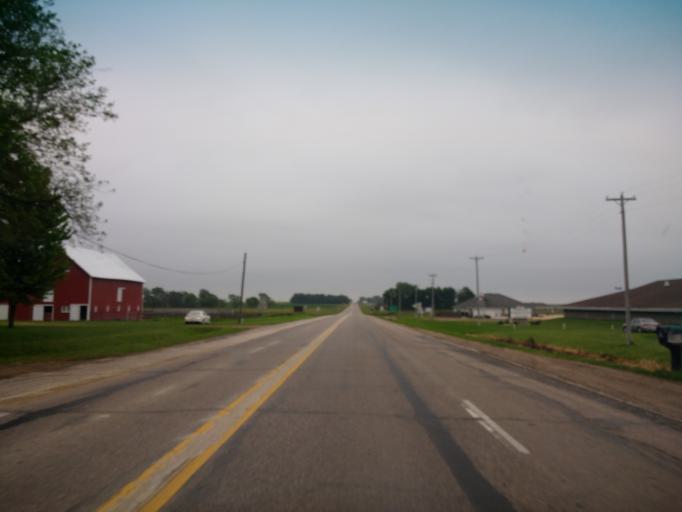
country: US
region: Iowa
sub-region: O'Brien County
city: Hartley
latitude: 43.1848
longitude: -95.4668
